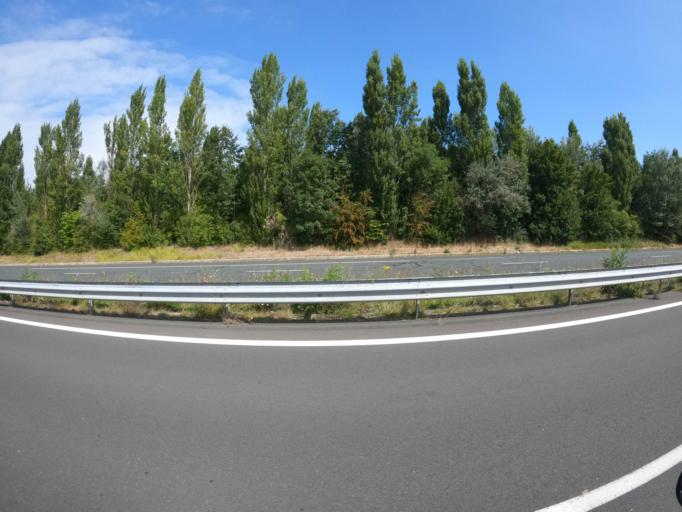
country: FR
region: Poitou-Charentes
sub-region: Departement de la Charente-Maritime
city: Courcon
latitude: 46.2114
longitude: -0.7565
